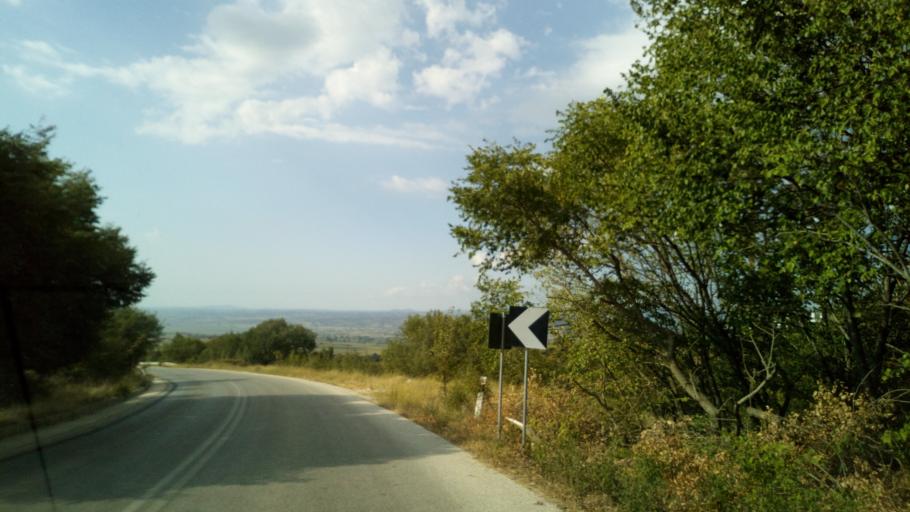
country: GR
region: Central Macedonia
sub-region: Nomos Thessalonikis
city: Gerakarou
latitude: 40.6166
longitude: 23.2235
